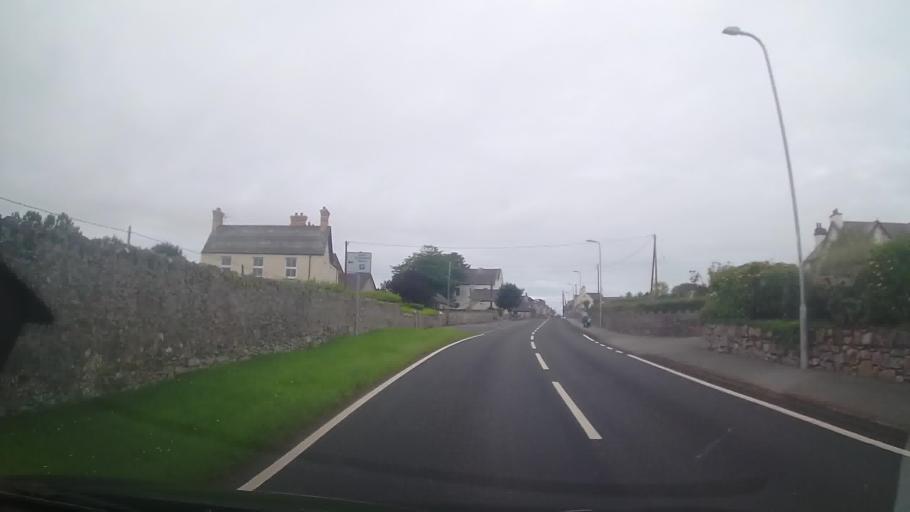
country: GB
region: Wales
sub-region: Gwynedd
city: Caernarfon
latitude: 53.1628
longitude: -4.3556
